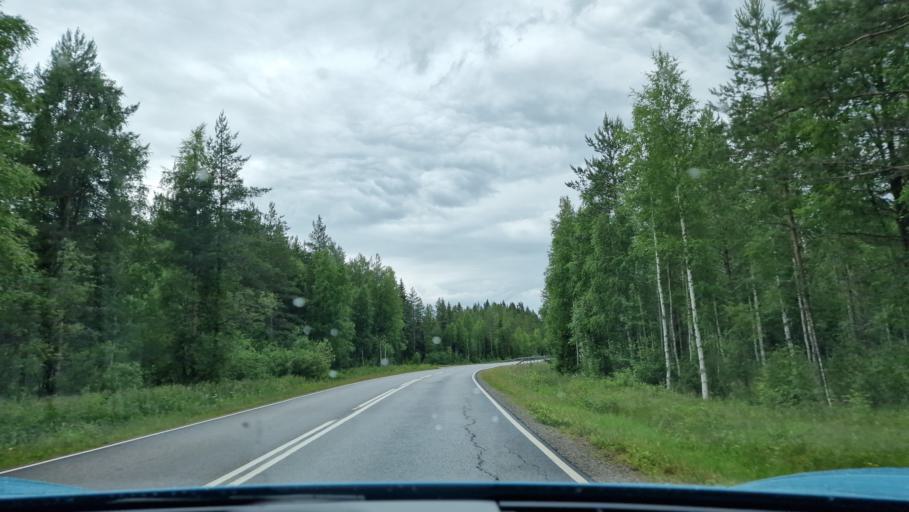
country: FI
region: Central Finland
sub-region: Saarijaervi-Viitasaari
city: Pylkoenmaeki
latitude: 62.6174
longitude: 24.5813
